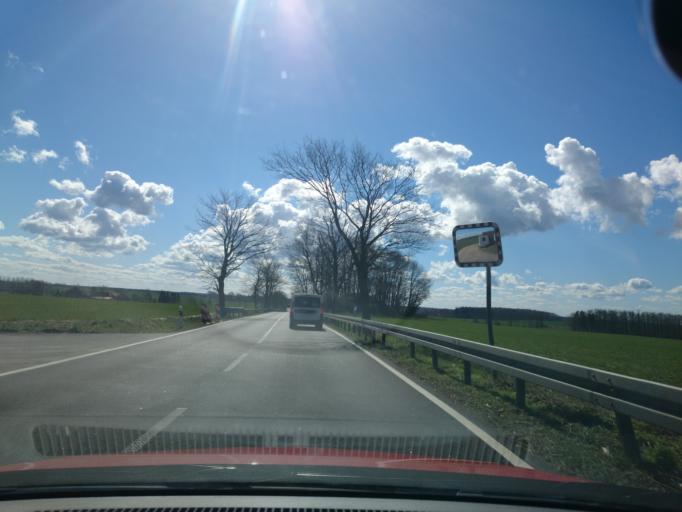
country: DE
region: Mecklenburg-Vorpommern
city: Barth
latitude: 54.3161
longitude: 12.7167
